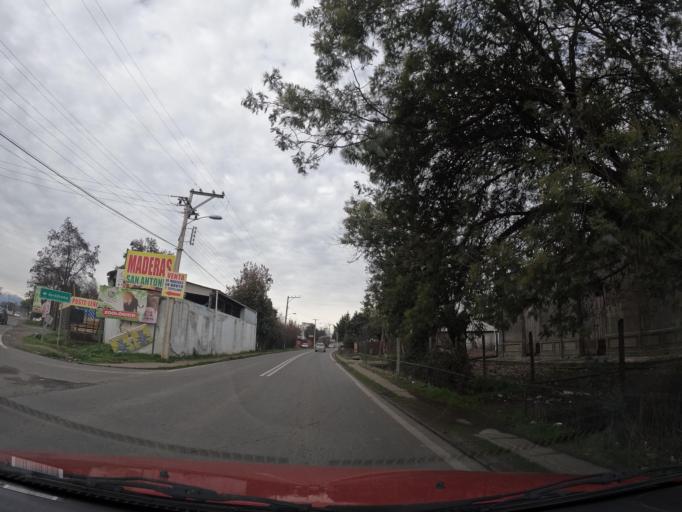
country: CL
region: Maule
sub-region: Provincia de Linares
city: Linares
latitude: -35.8673
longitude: -71.5522
